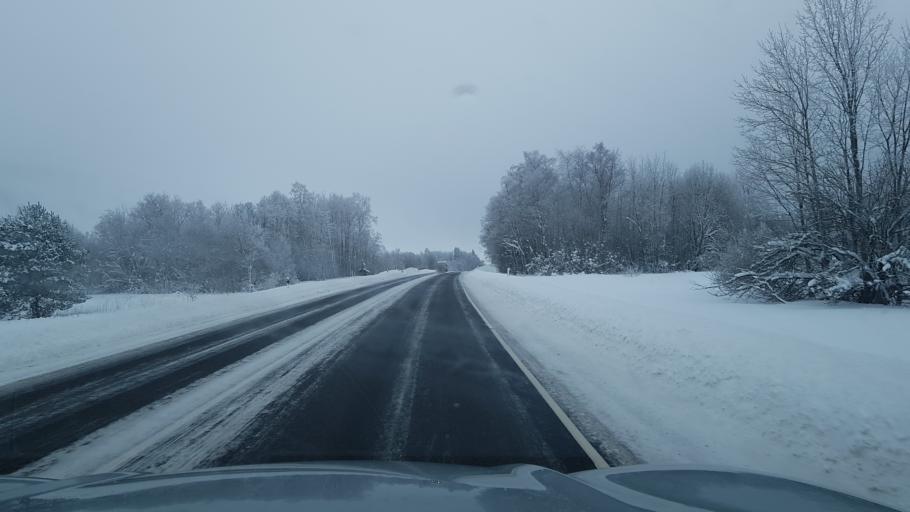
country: EE
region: Ida-Virumaa
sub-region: Johvi vald
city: Johvi
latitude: 59.2858
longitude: 27.3976
